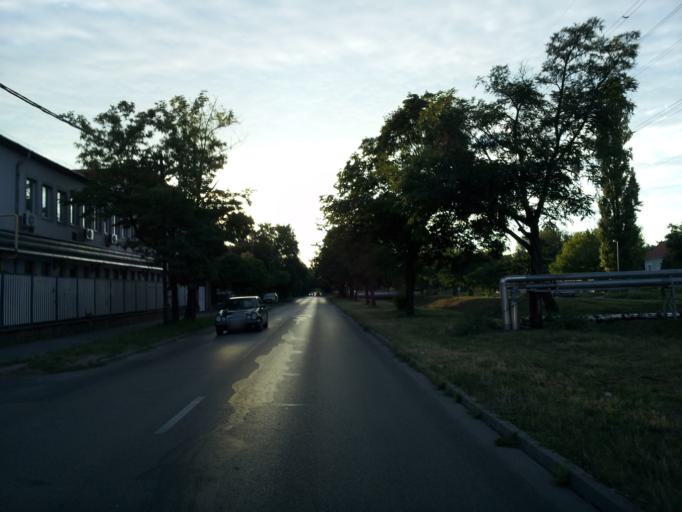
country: HU
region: Budapest
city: Budapest XIV. keruelet
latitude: 47.5254
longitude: 19.1151
